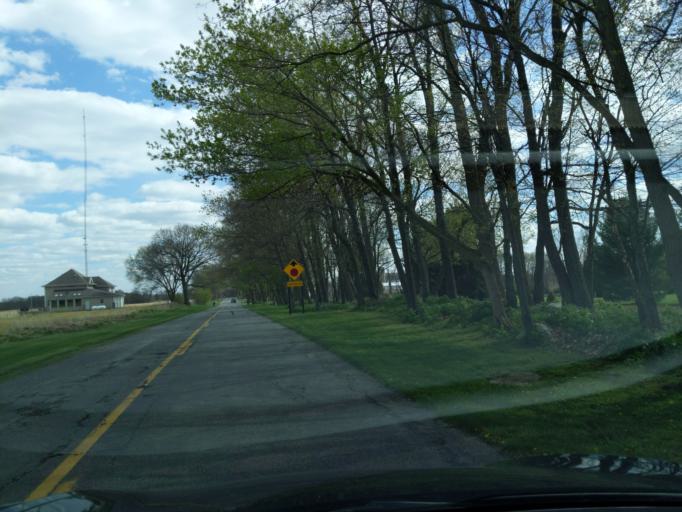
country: US
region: Michigan
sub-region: Ingham County
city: Leslie
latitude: 42.4283
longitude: -84.5263
